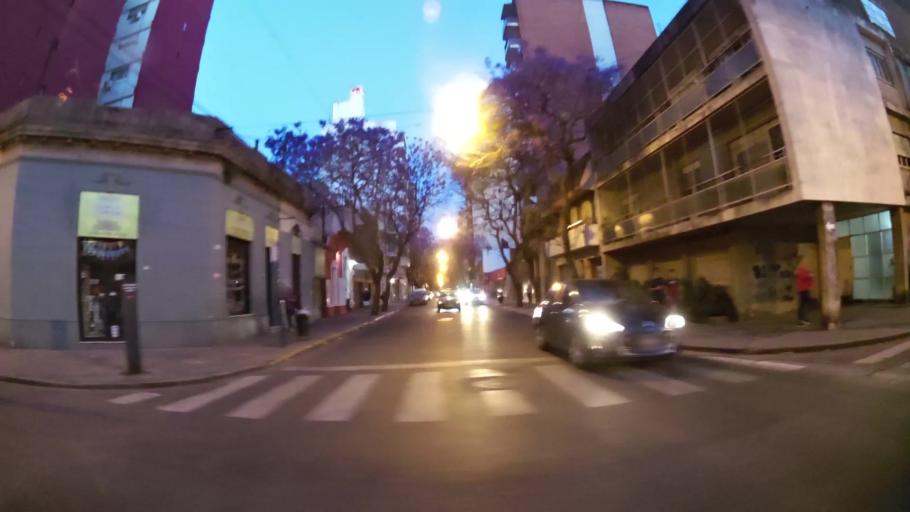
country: AR
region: Santa Fe
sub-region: Departamento de Rosario
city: Rosario
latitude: -32.9512
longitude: -60.6494
